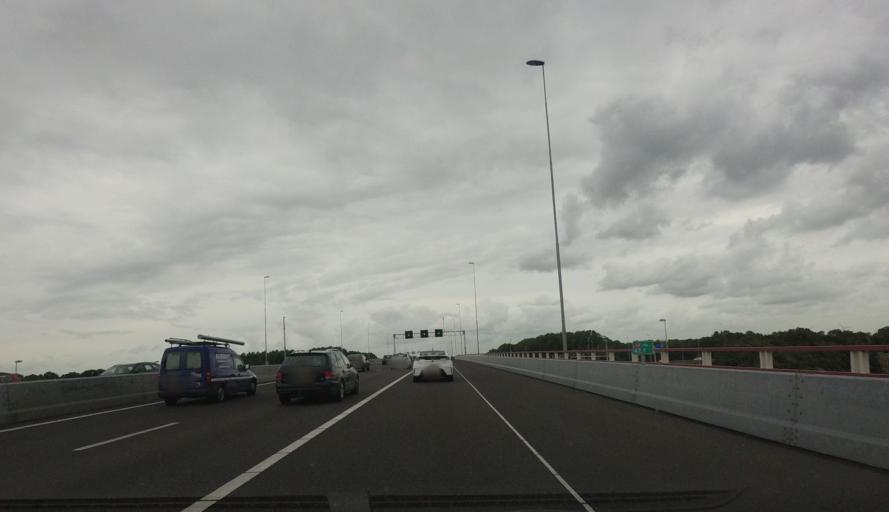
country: NL
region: North Holland
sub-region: Gemeente Haarlem
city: Haarlem
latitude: 52.3825
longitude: 4.7079
